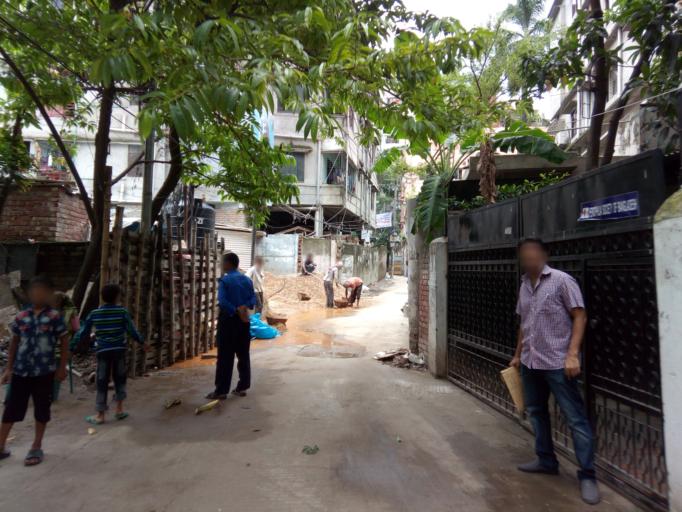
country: BD
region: Dhaka
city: Azimpur
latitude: 23.7518
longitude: 90.3802
